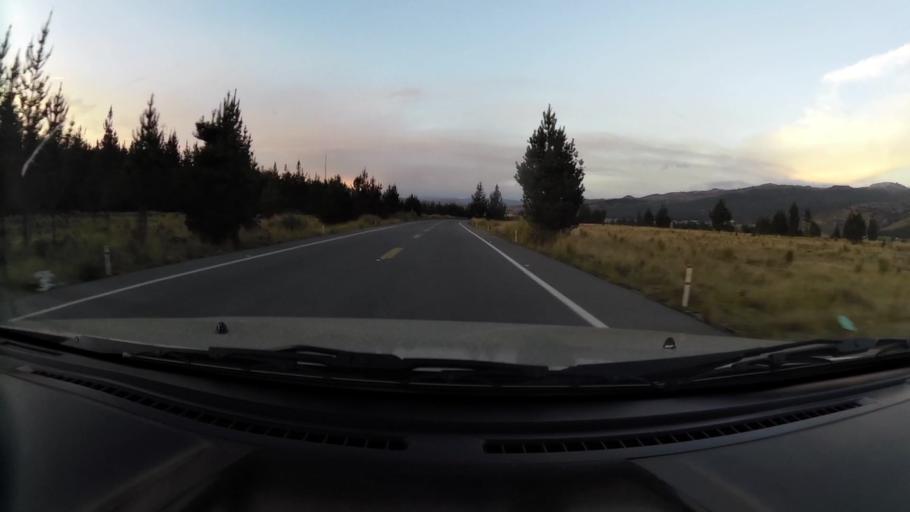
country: EC
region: Chimborazo
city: Alausi
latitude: -2.0287
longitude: -78.7349
